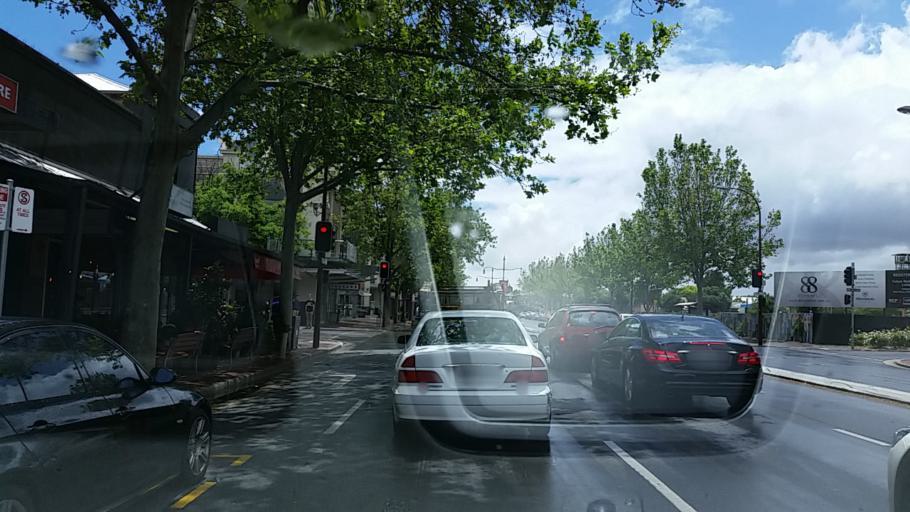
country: AU
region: South Australia
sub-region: Adelaide
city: North Adelaide
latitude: -34.9076
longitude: 138.5964
